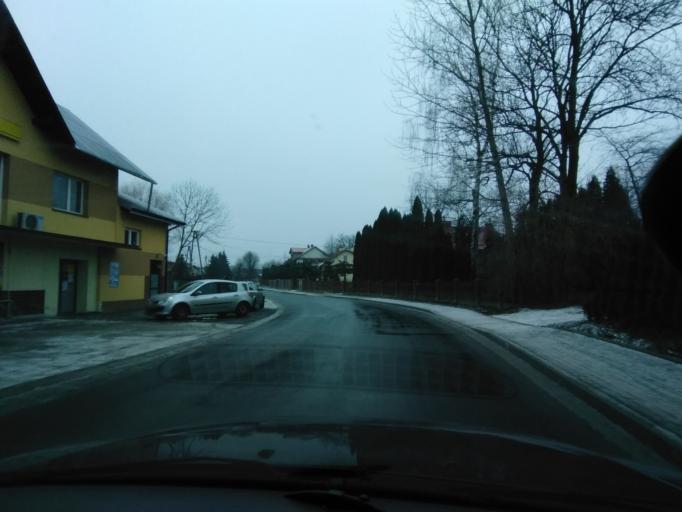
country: PL
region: Subcarpathian Voivodeship
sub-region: Powiat przeworski
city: Gac
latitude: 50.0249
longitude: 22.3912
